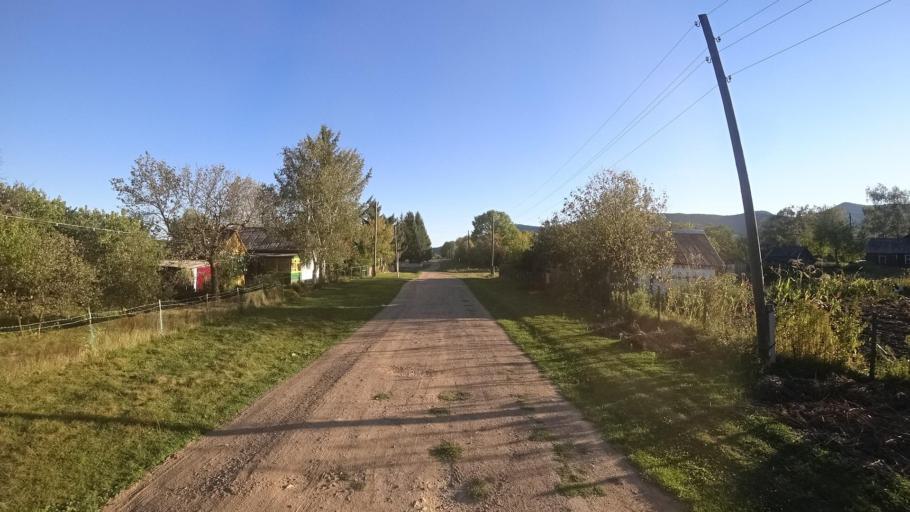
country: RU
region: Primorskiy
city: Kirovskiy
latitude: 44.8324
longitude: 133.5755
